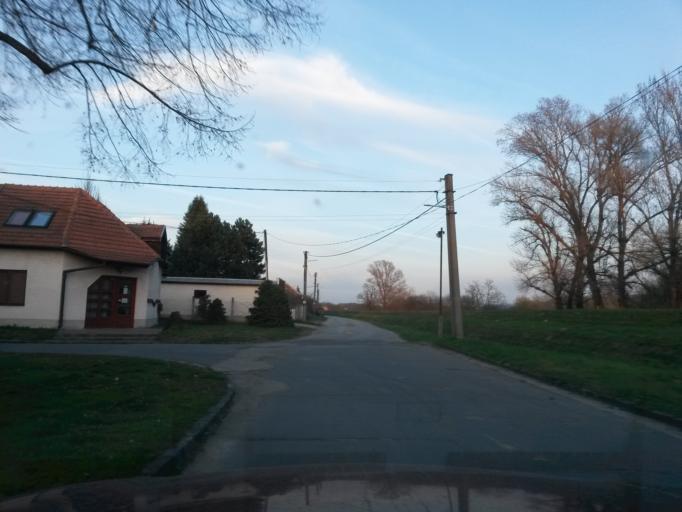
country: HU
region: Komarom-Esztergom
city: Almasfuzito
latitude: 47.7380
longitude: 18.2909
